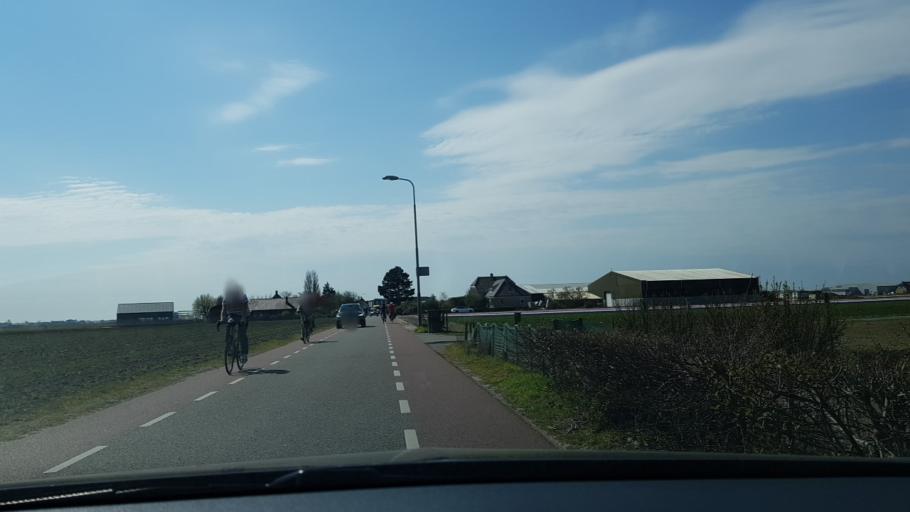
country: NL
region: South Holland
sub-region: Gemeente Teylingen
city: Sassenheim
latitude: 52.2518
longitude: 4.5243
